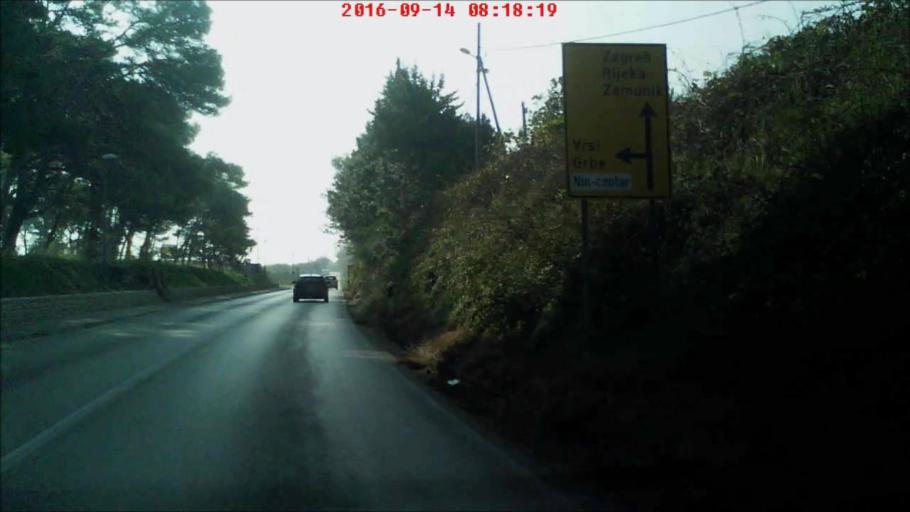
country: HR
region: Zadarska
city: Nin
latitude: 44.2388
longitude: 15.1838
